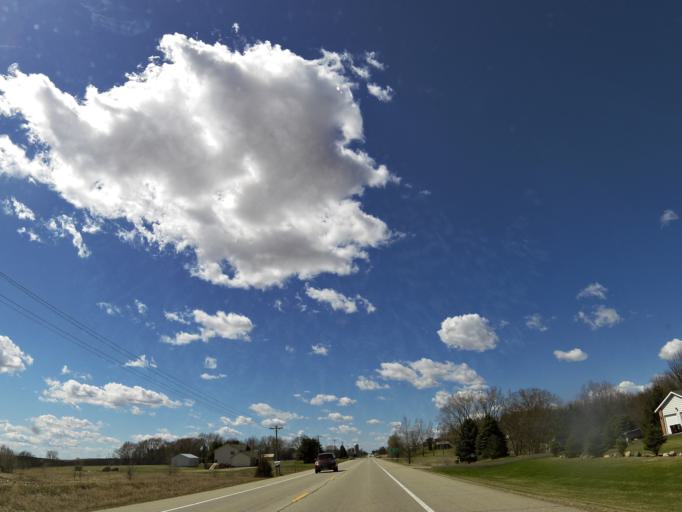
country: US
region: Minnesota
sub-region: Washington County
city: Cottage Grove
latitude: 44.7168
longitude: -92.9698
